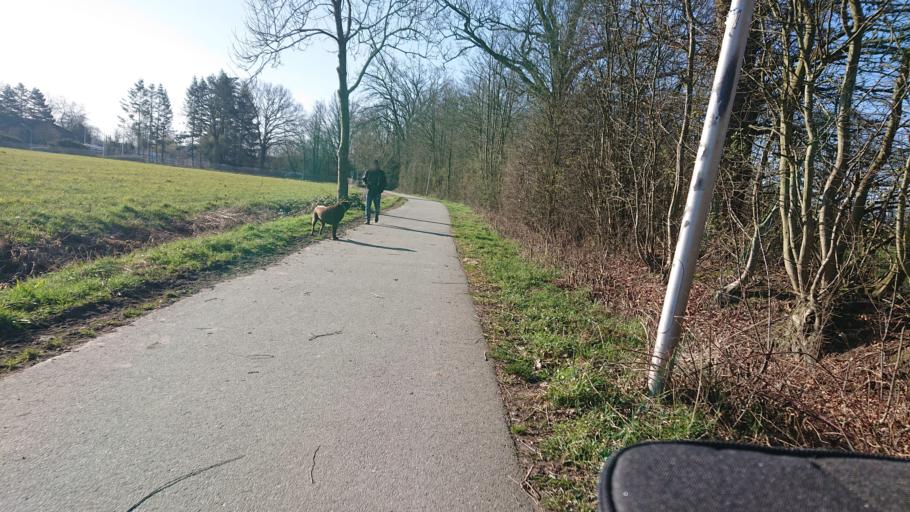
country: DE
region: Schleswig-Holstein
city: Ellerbek
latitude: 53.6492
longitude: 9.8855
